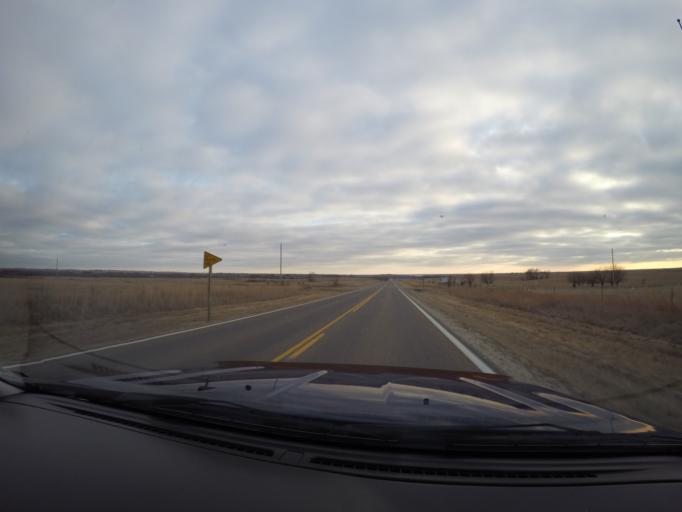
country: US
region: Kansas
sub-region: Morris County
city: Council Grove
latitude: 38.7543
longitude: -96.5012
